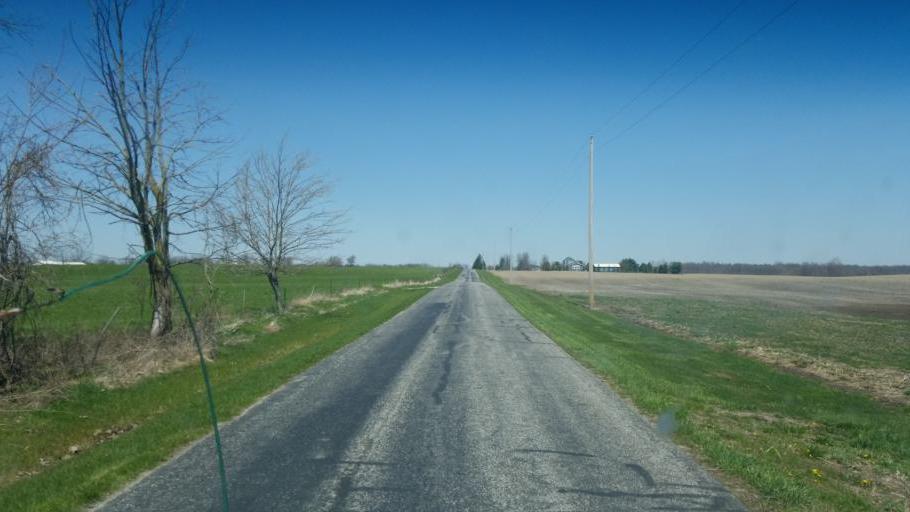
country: US
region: Ohio
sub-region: Huron County
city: New London
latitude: 41.0814
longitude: -82.4377
